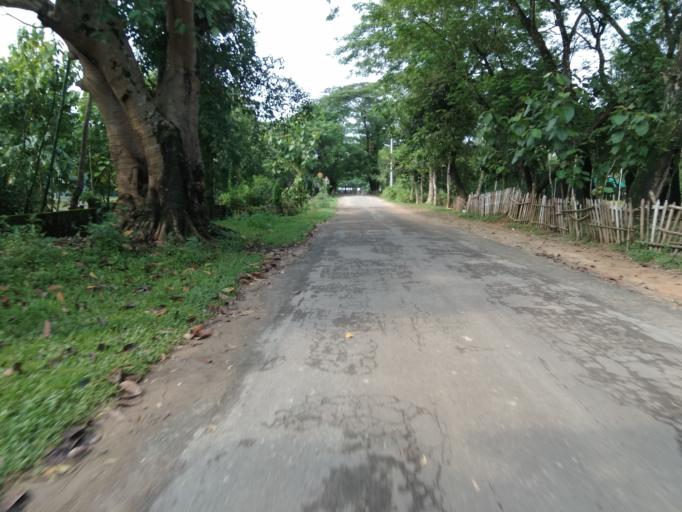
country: BD
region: Chittagong
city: Khagrachhari
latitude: 23.0195
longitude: 92.0134
